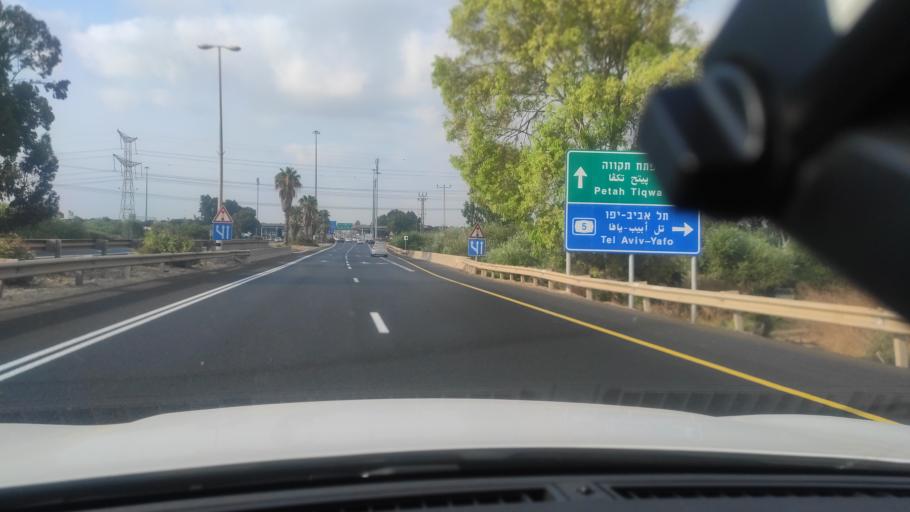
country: IL
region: Central District
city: Hod HaSharon
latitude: 32.1252
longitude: 34.9039
